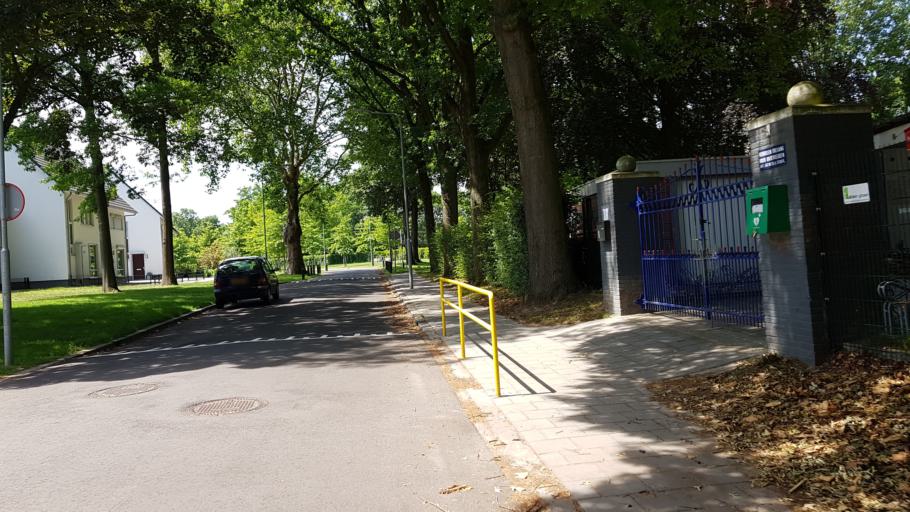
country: NL
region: Limburg
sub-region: Gemeente Sittard-Geleen
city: Sittard
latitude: 50.9945
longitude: 5.8541
